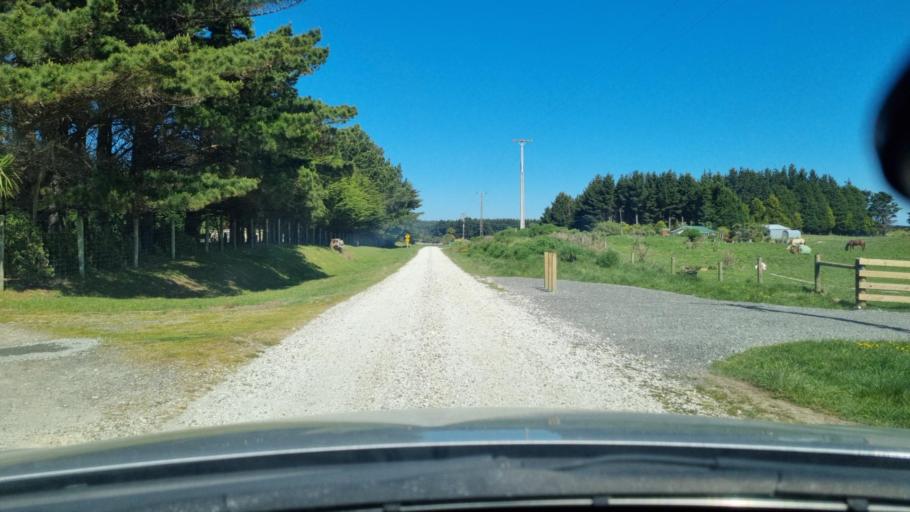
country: NZ
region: Southland
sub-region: Invercargill City
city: Invercargill
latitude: -46.4569
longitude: 168.2725
